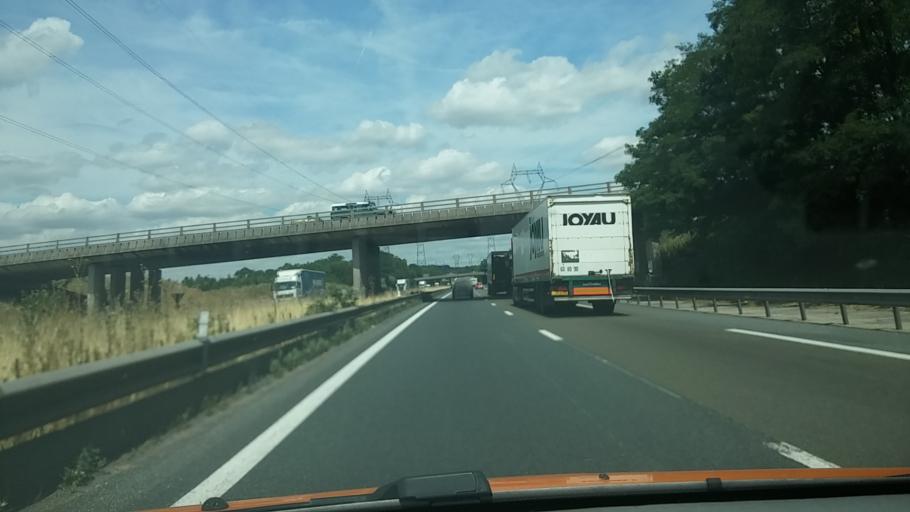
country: FR
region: Ile-de-France
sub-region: Departement de Seine-et-Marne
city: Le Pin
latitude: 48.9098
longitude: 2.6371
